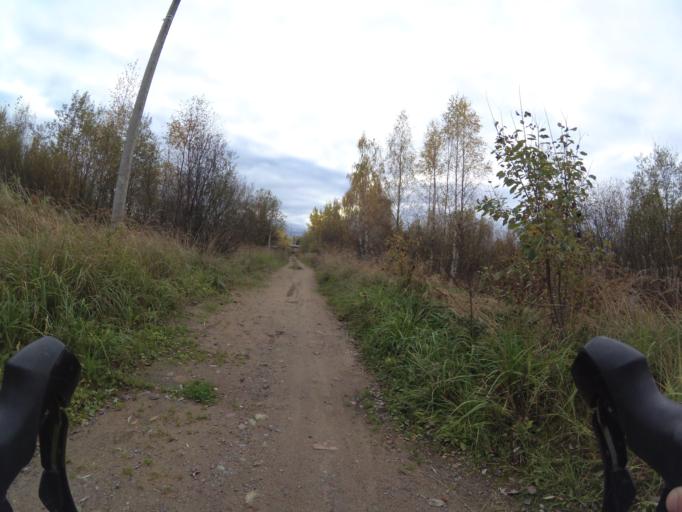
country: RU
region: St.-Petersburg
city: Lakhtinskiy
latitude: 60.0066
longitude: 30.1446
